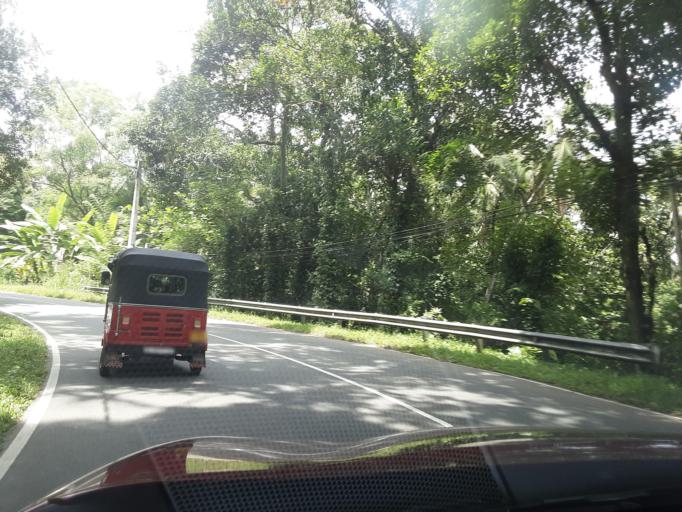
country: LK
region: Uva
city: Monaragala
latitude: 6.8958
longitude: 81.2525
